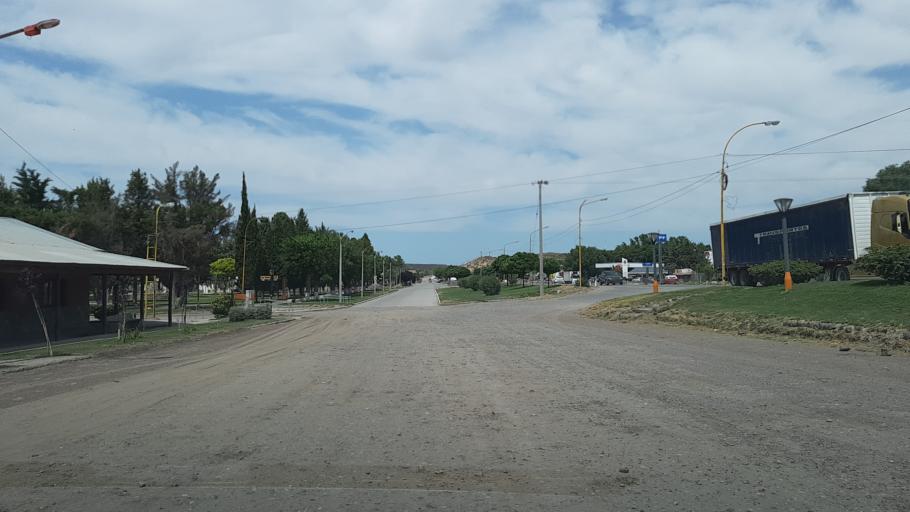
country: AR
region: Neuquen
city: Piedra del Aguila
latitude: -40.0474
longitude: -70.0747
